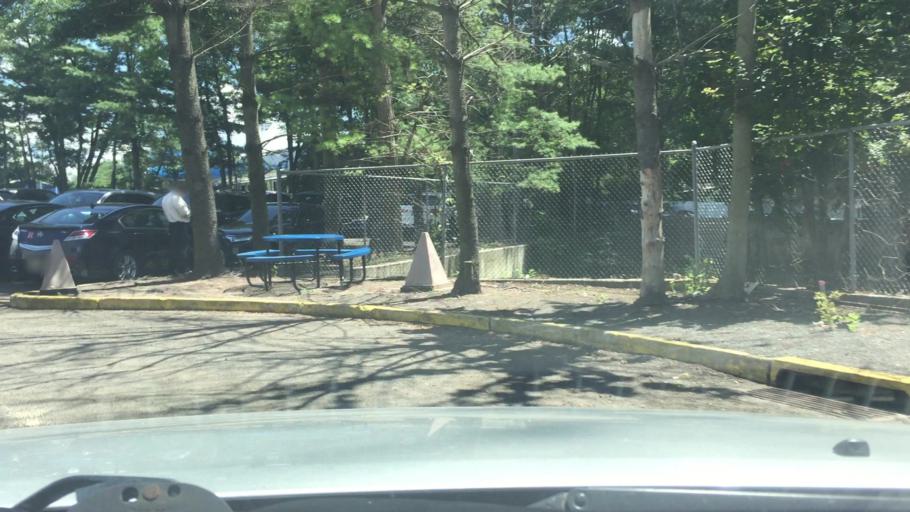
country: US
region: New Jersey
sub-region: Middlesex County
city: Old Bridge
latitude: 40.4164
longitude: -74.3728
